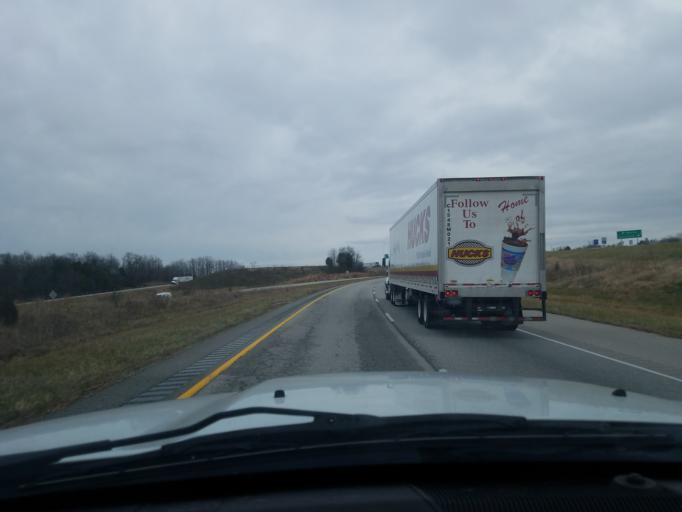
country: US
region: Indiana
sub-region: Crawford County
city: English
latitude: 38.2414
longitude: -86.3633
